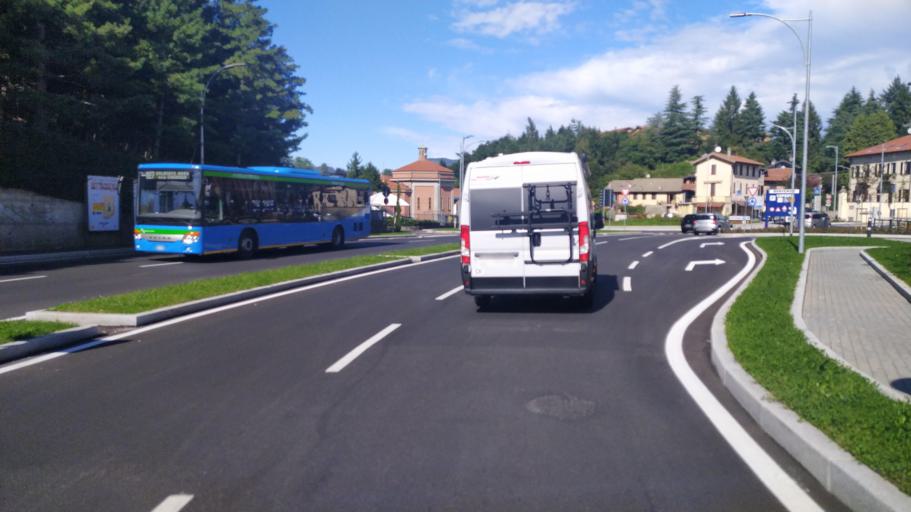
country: IT
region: Lombardy
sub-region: Provincia di Varese
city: Gazzada Schianno
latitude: 45.8009
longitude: 8.8339
